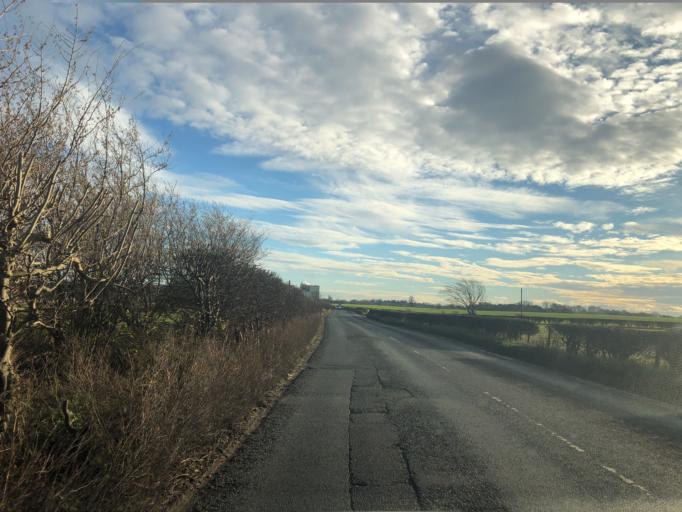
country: GB
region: England
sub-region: North Yorkshire
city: Thirsk
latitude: 54.1755
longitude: -1.3685
